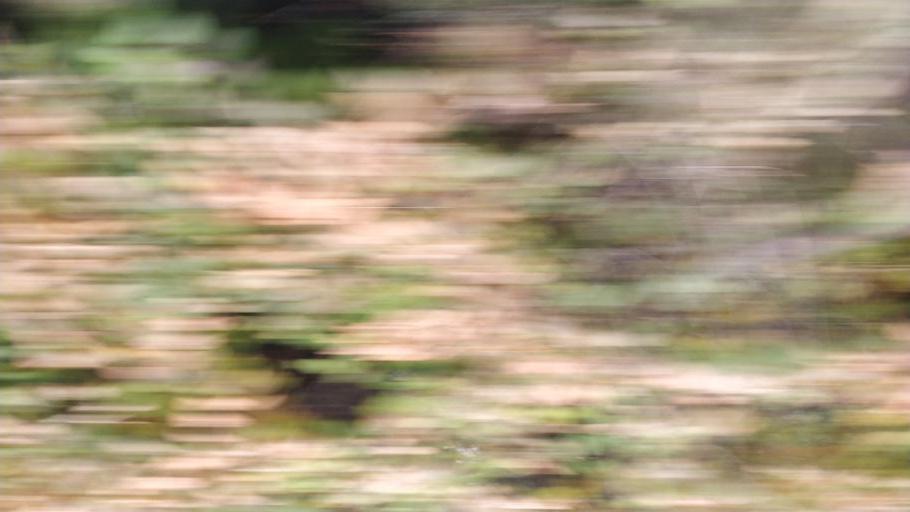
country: GB
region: England
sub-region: City and Borough of Salford
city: Salford
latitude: 53.4915
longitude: -2.2802
